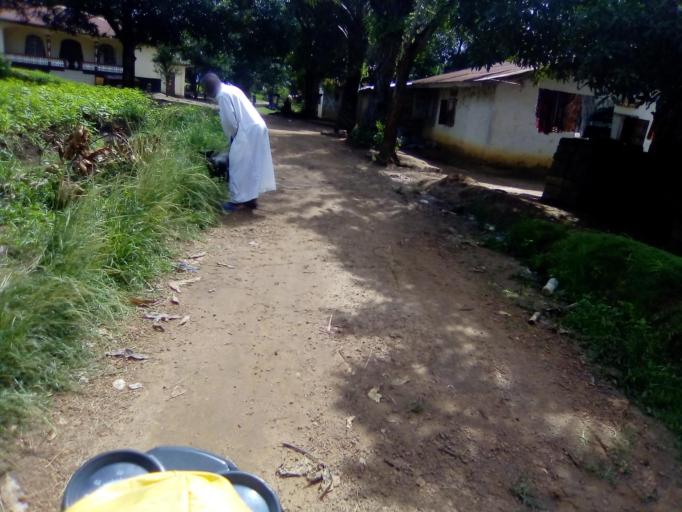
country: SL
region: Southern Province
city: Baoma
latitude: 7.9813
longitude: -11.7252
